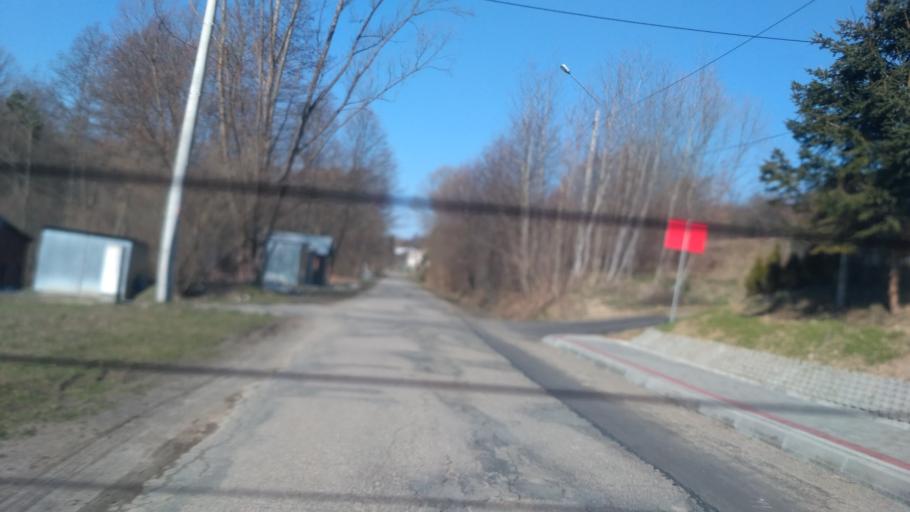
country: PL
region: Subcarpathian Voivodeship
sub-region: Powiat strzyzowski
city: Gwoznica Gorna
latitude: 49.8159
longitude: 22.0273
